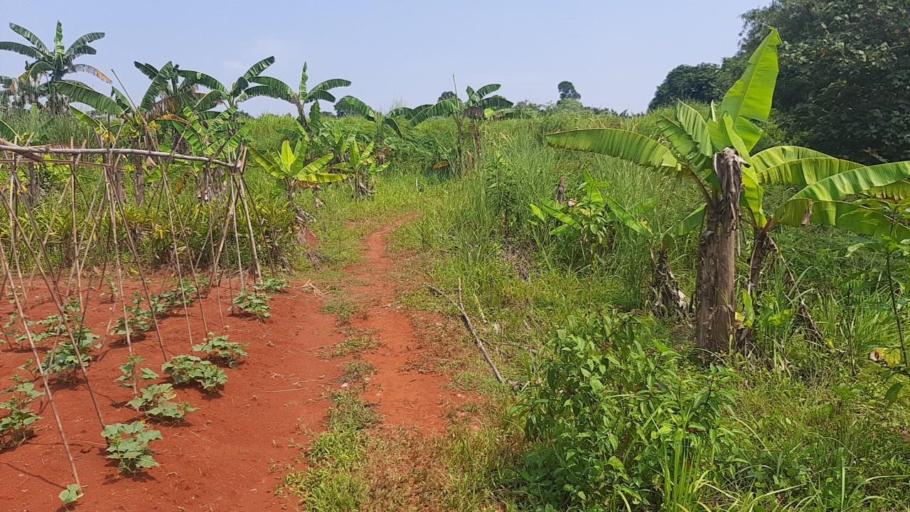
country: ID
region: West Java
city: Cileungsir
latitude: -6.3457
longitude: 106.9584
